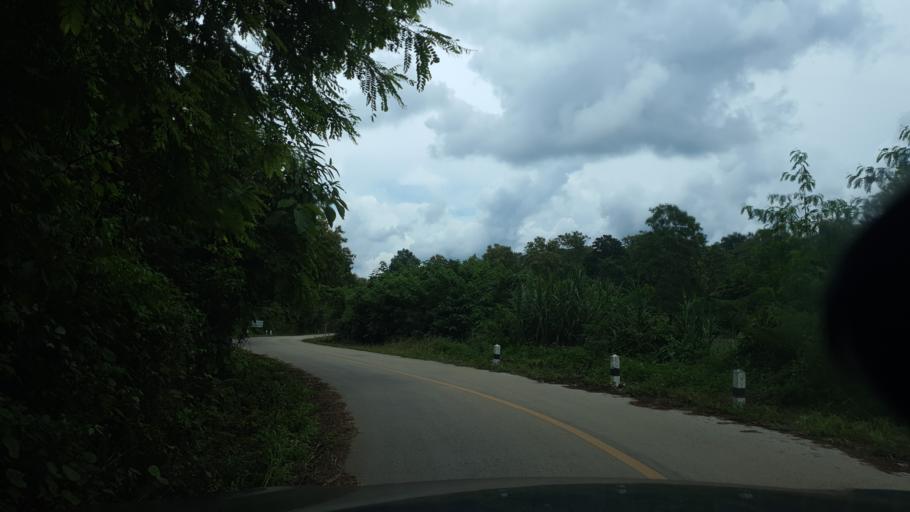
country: TH
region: Lampang
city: Hang Chat
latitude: 18.3700
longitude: 99.2605
